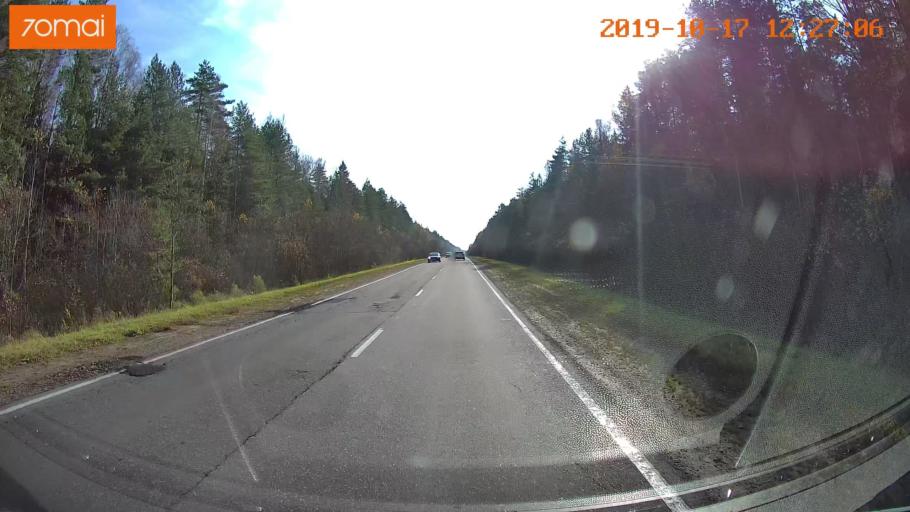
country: RU
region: Rjazan
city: Syntul
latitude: 55.0099
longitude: 41.2603
